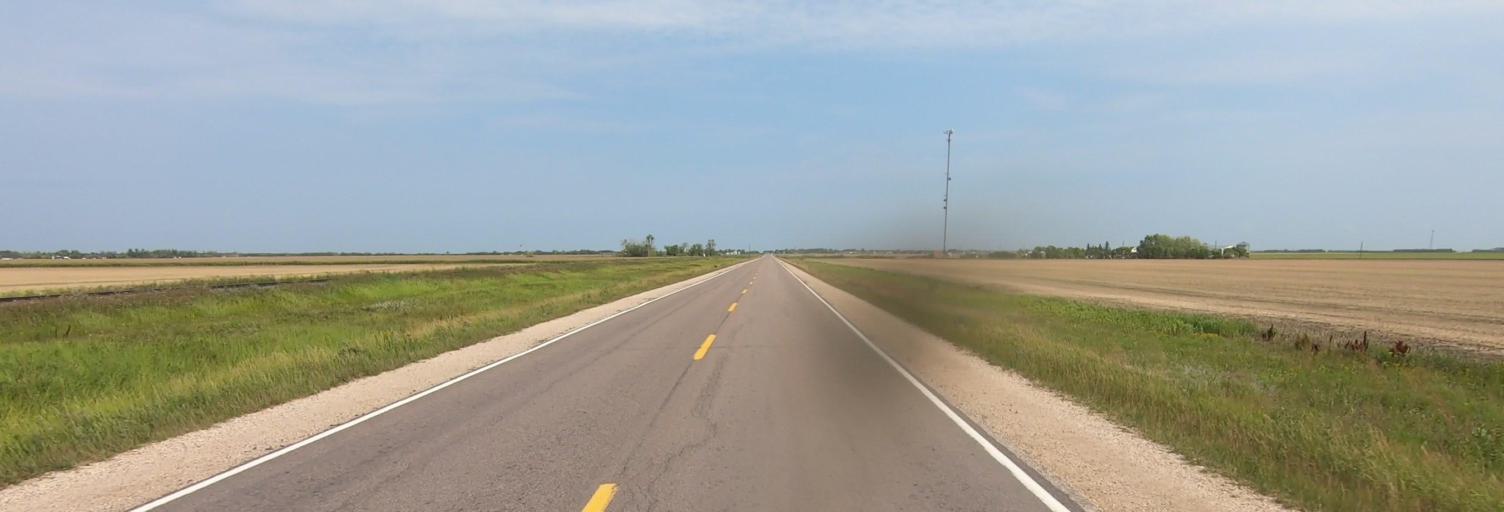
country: CA
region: Manitoba
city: Headingley
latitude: 49.6667
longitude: -97.2831
